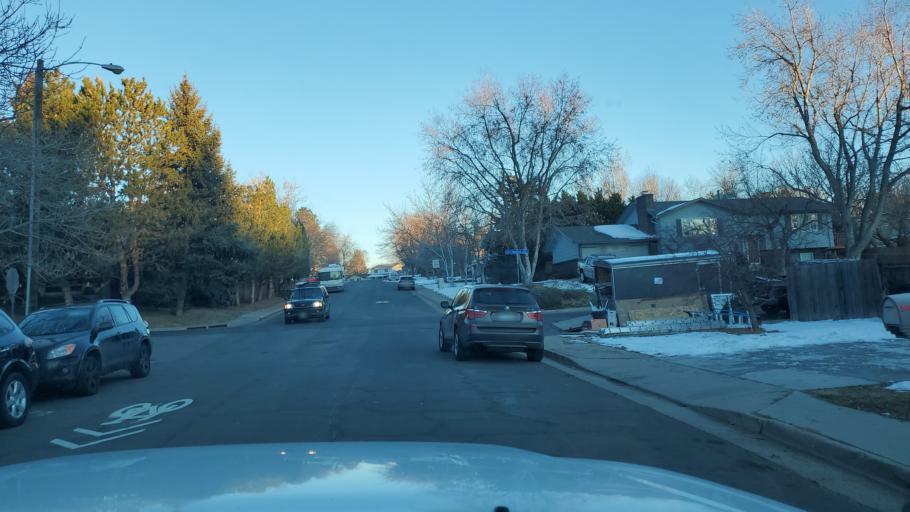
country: US
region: Colorado
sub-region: Arapahoe County
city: Castlewood
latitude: 39.5916
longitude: -104.9038
